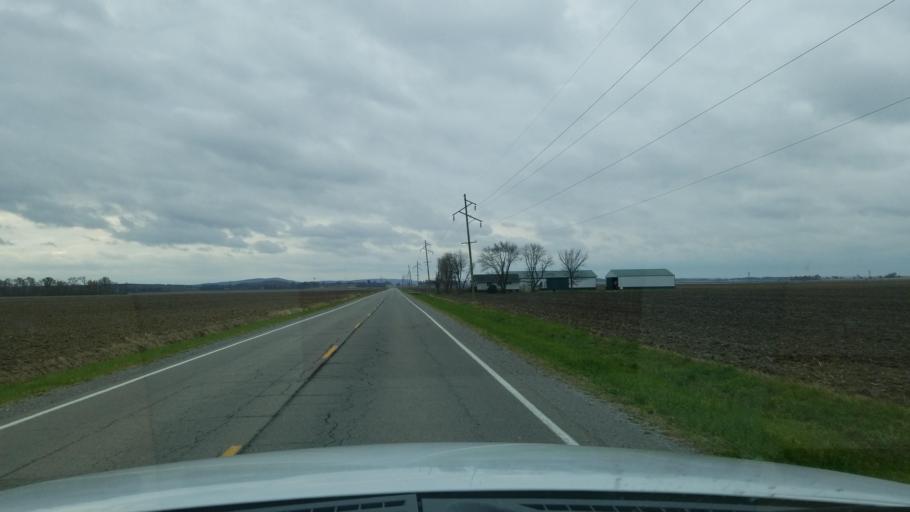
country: US
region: Illinois
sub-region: Saline County
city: Eldorado
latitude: 37.7852
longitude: -88.4382
